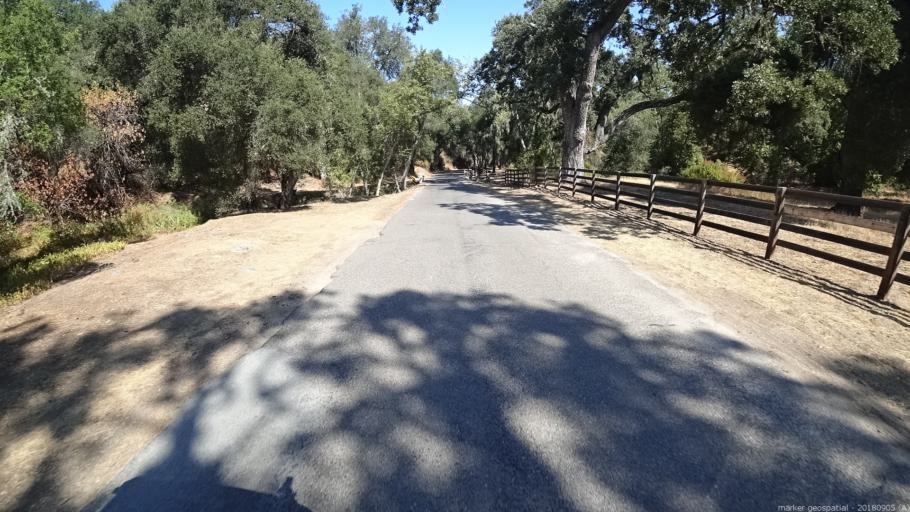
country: US
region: California
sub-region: Monterey County
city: Gonzales
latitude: 36.3771
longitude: -121.5919
